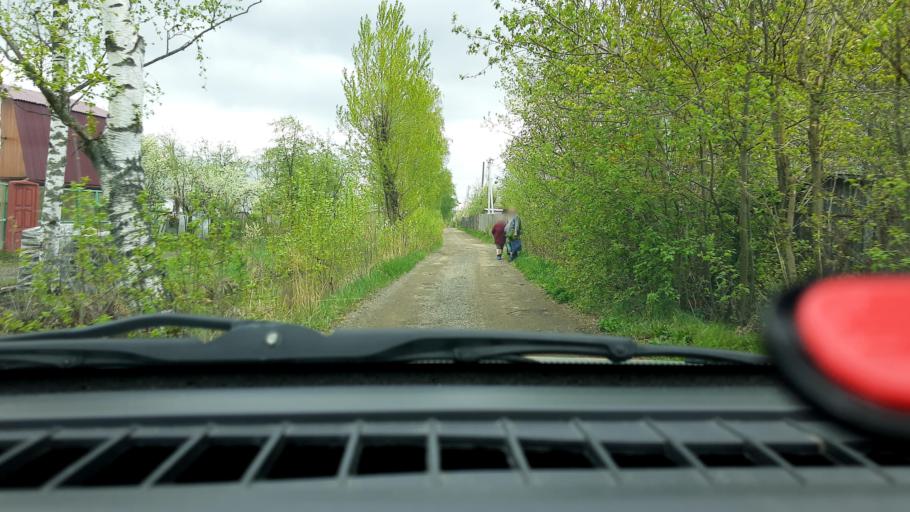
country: RU
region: Nizjnij Novgorod
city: Gorbatovka
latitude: 56.2402
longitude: 43.8139
